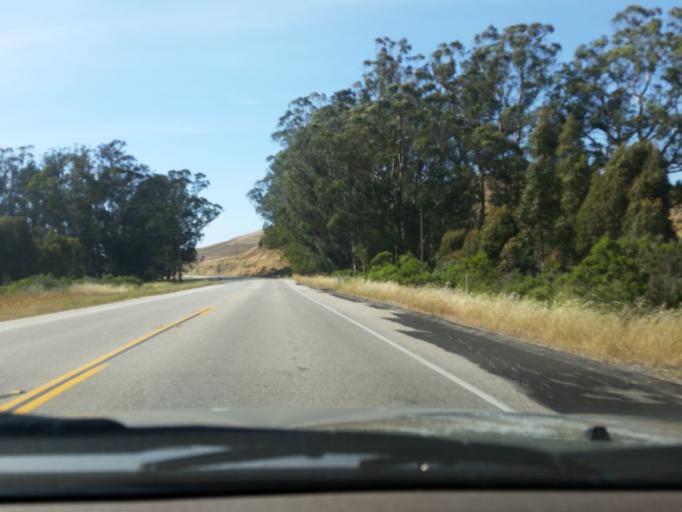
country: US
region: California
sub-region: San Luis Obispo County
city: Cayucos
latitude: 35.4851
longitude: -120.9979
